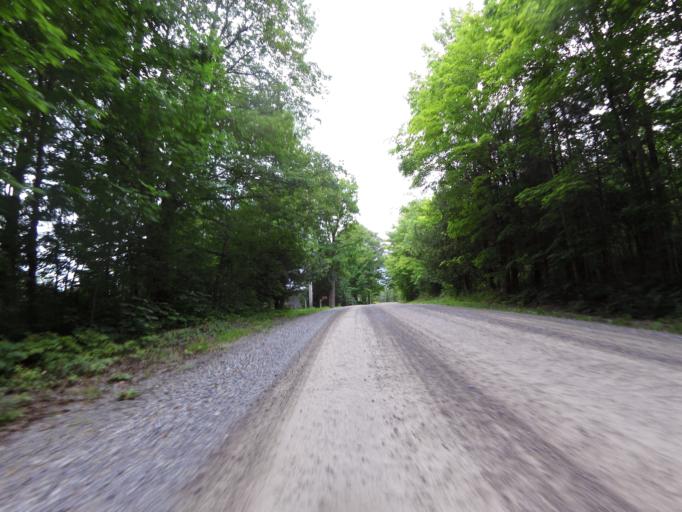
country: CA
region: Ontario
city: Carleton Place
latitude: 45.1547
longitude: -76.2085
